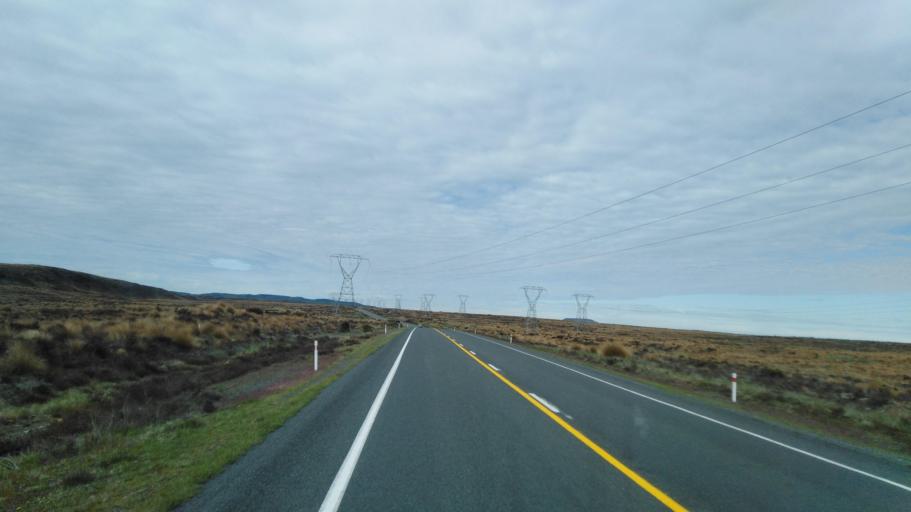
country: NZ
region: Manawatu-Wanganui
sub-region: Ruapehu District
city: Waiouru
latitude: -39.3968
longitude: 175.7002
